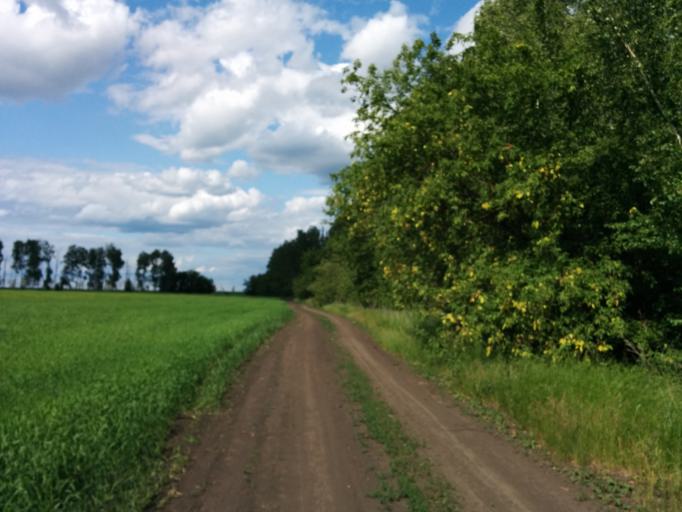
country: RU
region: Tambov
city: Tambov
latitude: 52.8036
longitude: 41.3898
